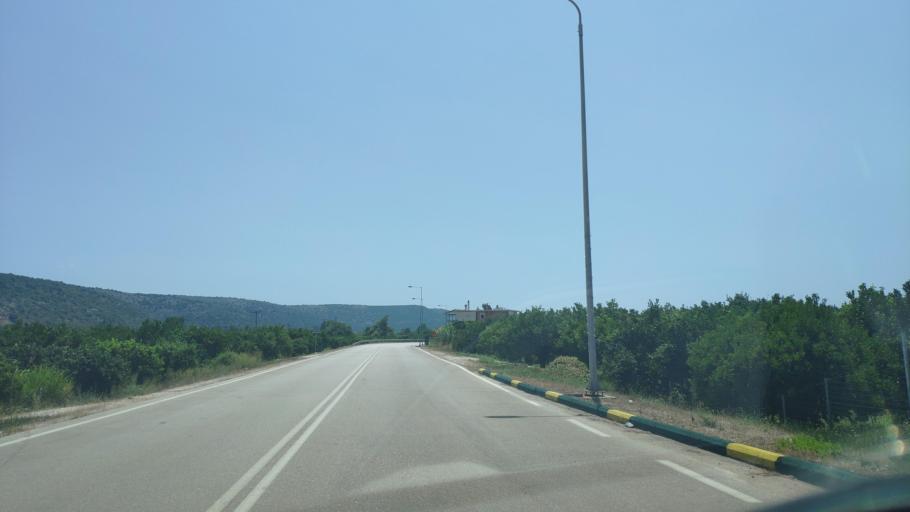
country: GR
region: Epirus
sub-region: Nomos Artas
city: Arta
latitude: 39.1419
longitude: 20.9804
